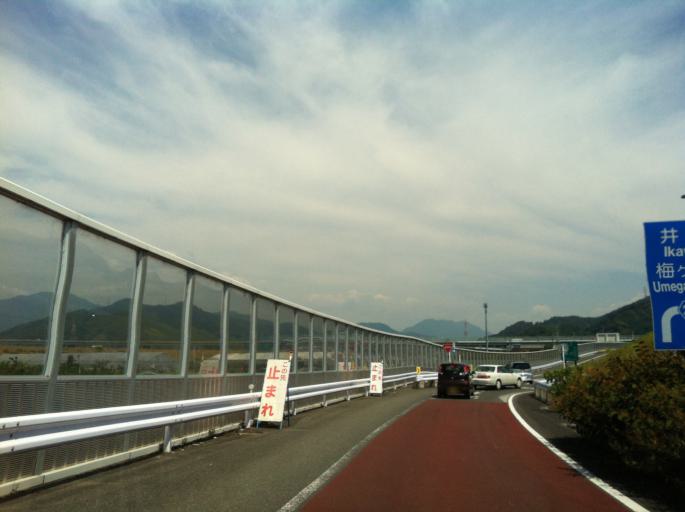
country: JP
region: Shizuoka
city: Shizuoka-shi
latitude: 35.0348
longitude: 138.3776
